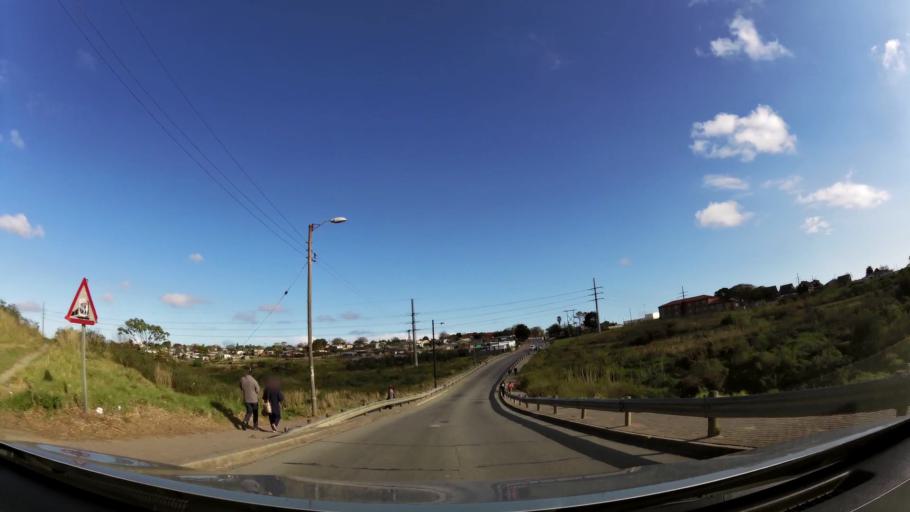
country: ZA
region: Western Cape
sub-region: Eden District Municipality
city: George
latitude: -33.9791
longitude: 22.4769
